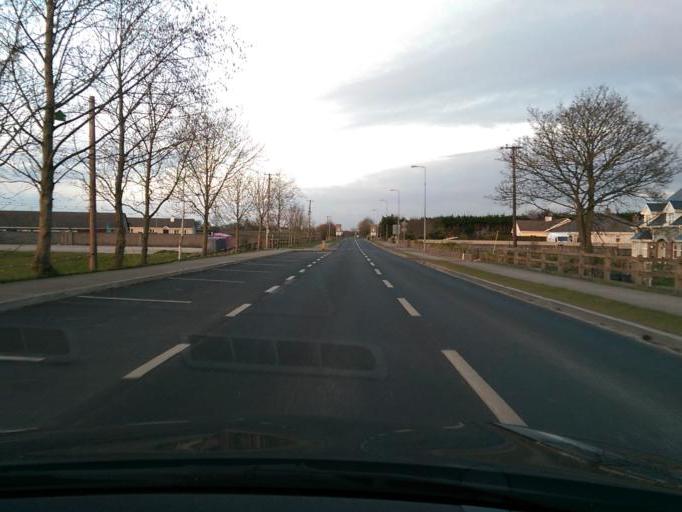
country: IE
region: Munster
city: Nenagh Bridge
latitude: 52.9367
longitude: -8.1543
